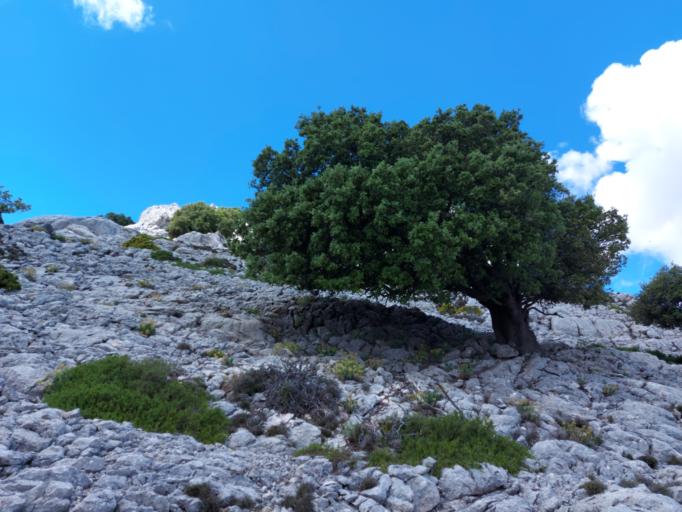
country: ES
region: Balearic Islands
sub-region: Illes Balears
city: Escorca
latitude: 39.8048
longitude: 2.8680
